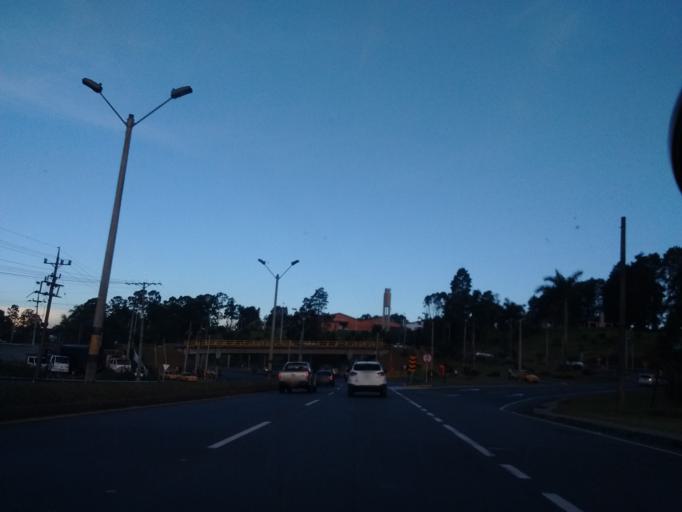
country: CO
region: Antioquia
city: Rionegro
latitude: 6.1798
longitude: -75.3684
